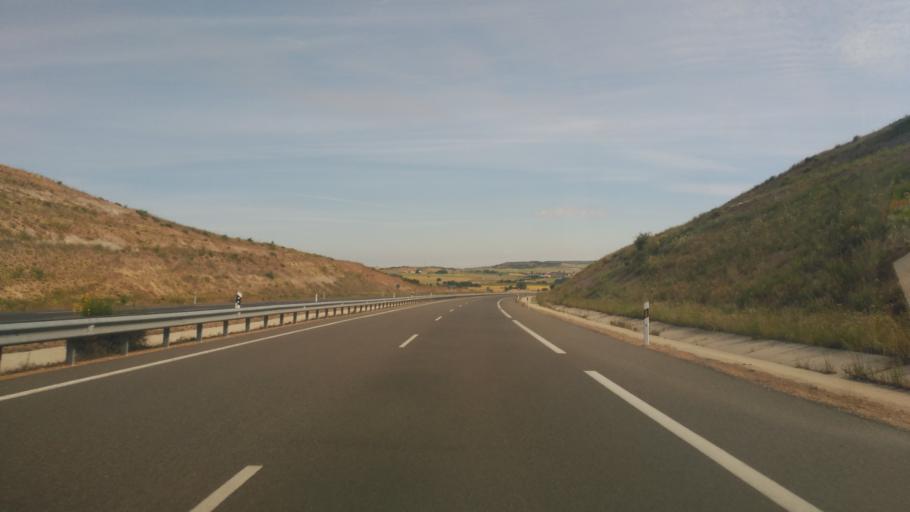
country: ES
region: Castille and Leon
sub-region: Provincia de Zamora
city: Corrales
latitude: 41.3251
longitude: -5.7264
